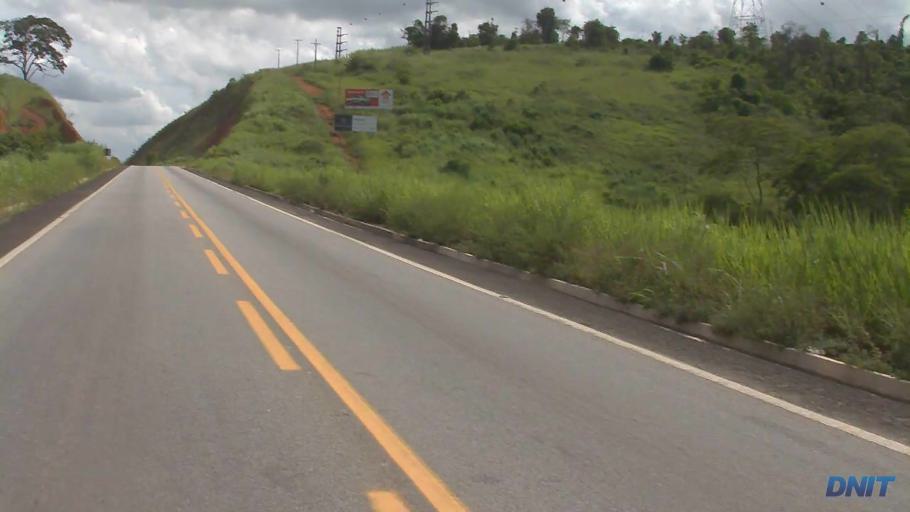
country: BR
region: Minas Gerais
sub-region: Ipatinga
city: Ipatinga
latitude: -19.4160
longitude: -42.4923
